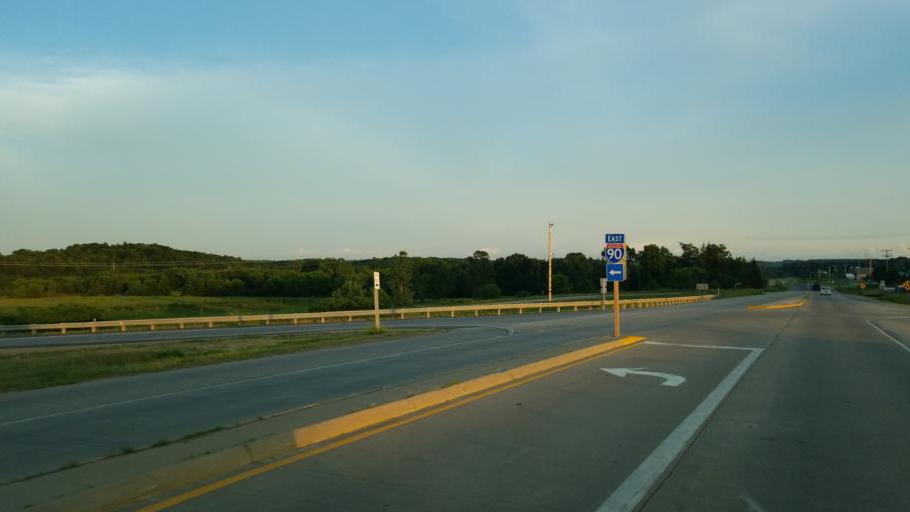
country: US
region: Wisconsin
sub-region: Monroe County
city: Tomah
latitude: 43.9568
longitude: -90.5048
